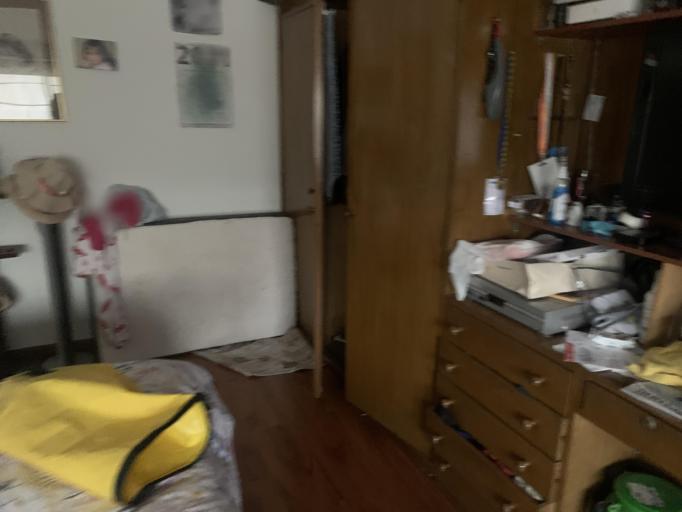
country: CO
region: Bogota D.C.
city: Barrio San Luis
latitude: 4.7106
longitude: -74.0700
